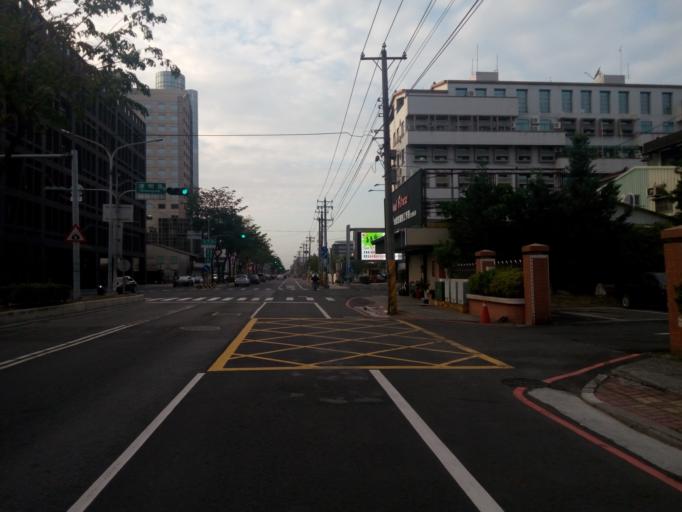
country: TW
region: Taiwan
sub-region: Chiayi
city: Jiayi Shi
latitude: 23.4794
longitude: 120.4315
